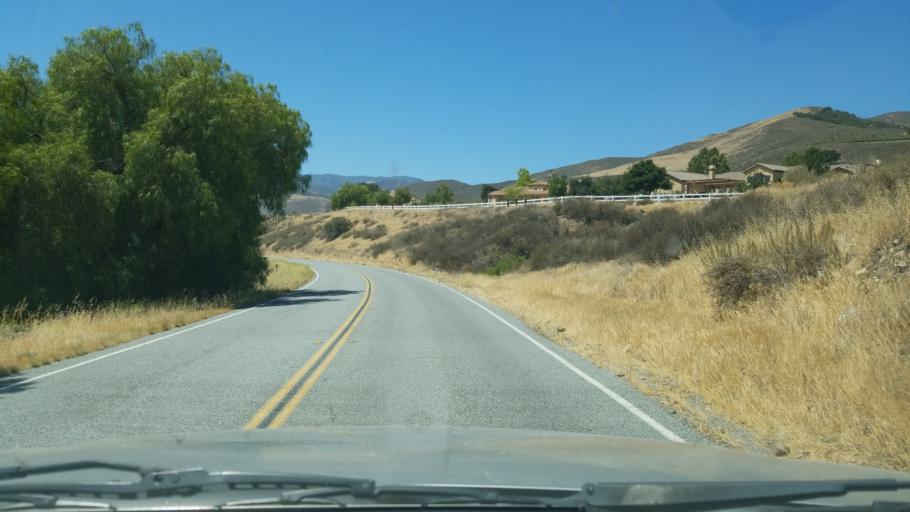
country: US
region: California
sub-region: Monterey County
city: Greenfield
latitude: 36.2865
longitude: -121.3194
